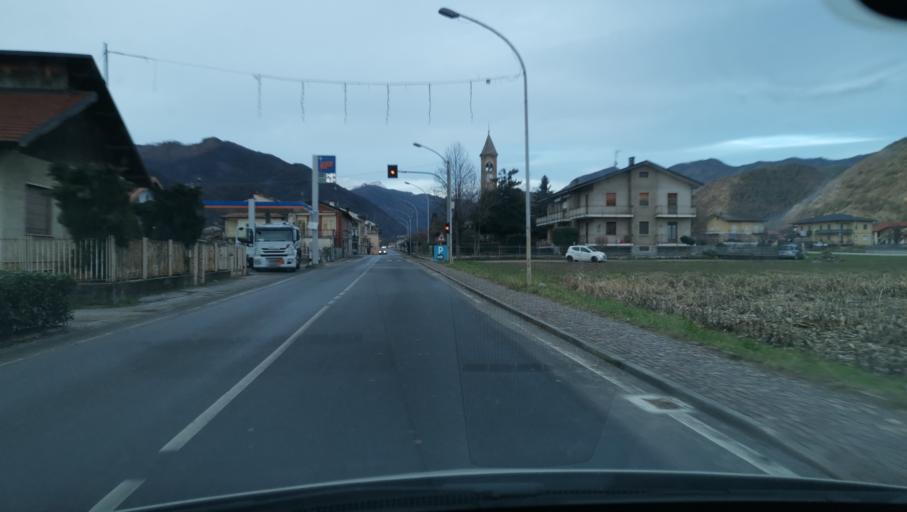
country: IT
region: Piedmont
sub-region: Provincia di Cuneo
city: Valgrana
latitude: 44.4128
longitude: 7.3833
